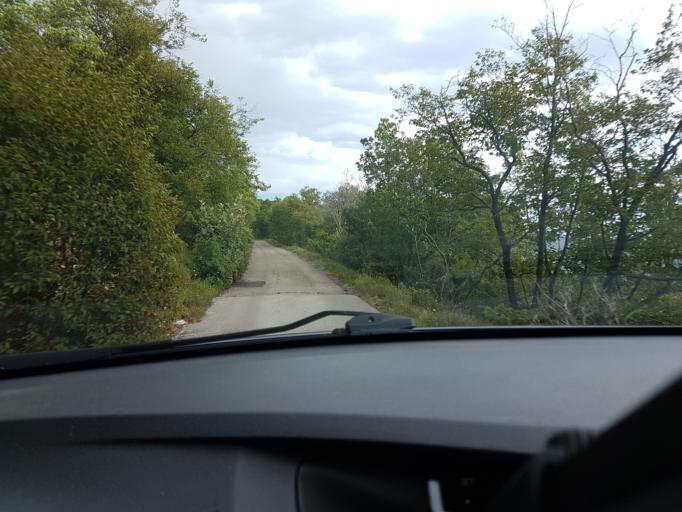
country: HR
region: Primorsko-Goranska
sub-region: Grad Crikvenica
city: Crikvenica
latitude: 45.2306
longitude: 14.7042
